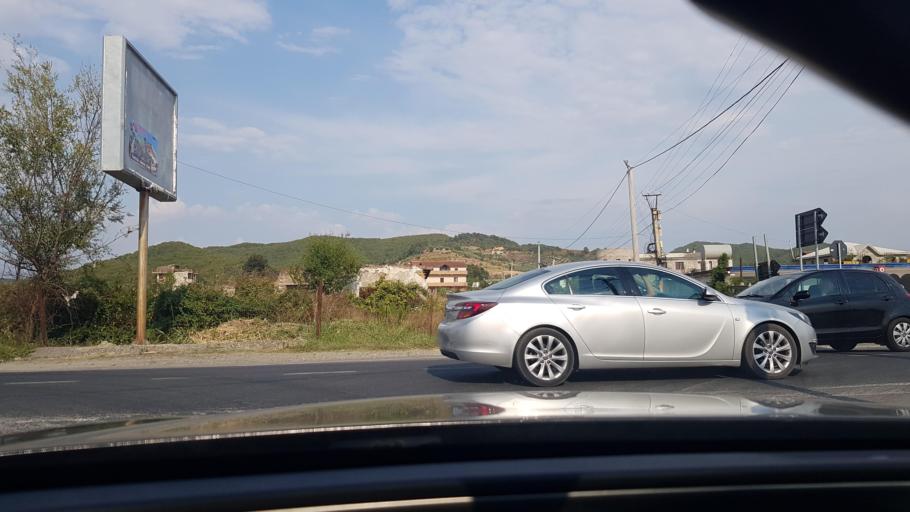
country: AL
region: Durres
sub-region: Rrethi i Durresit
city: Manze
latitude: 41.4746
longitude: 19.5613
